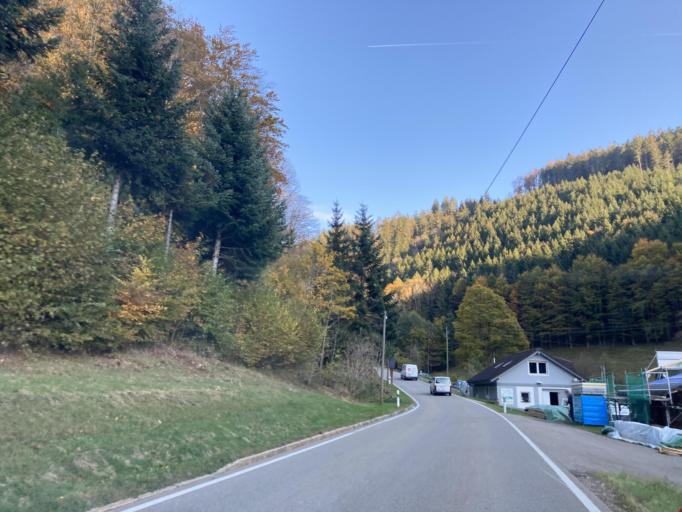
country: DE
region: Baden-Wuerttemberg
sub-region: Freiburg Region
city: Breitnau
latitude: 47.9684
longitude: 8.0789
